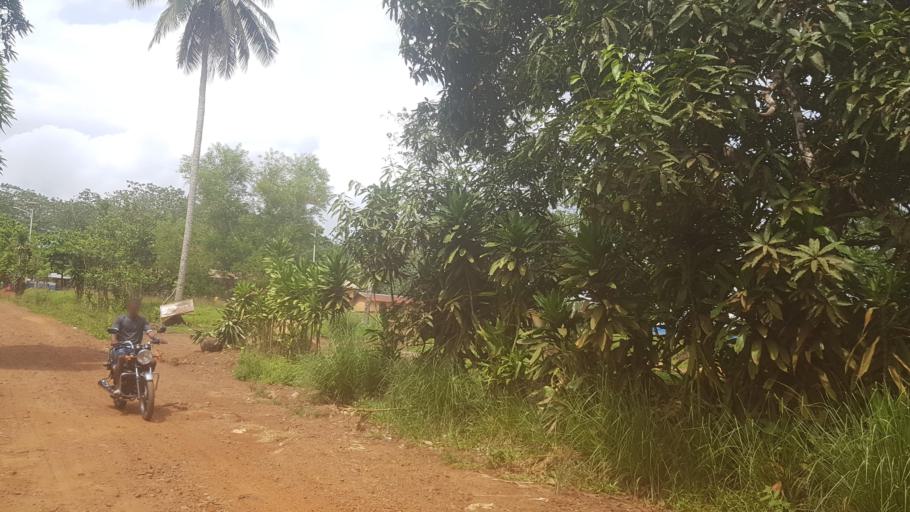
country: SL
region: Southern Province
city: Mogbwemo
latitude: 7.6022
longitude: -12.1760
